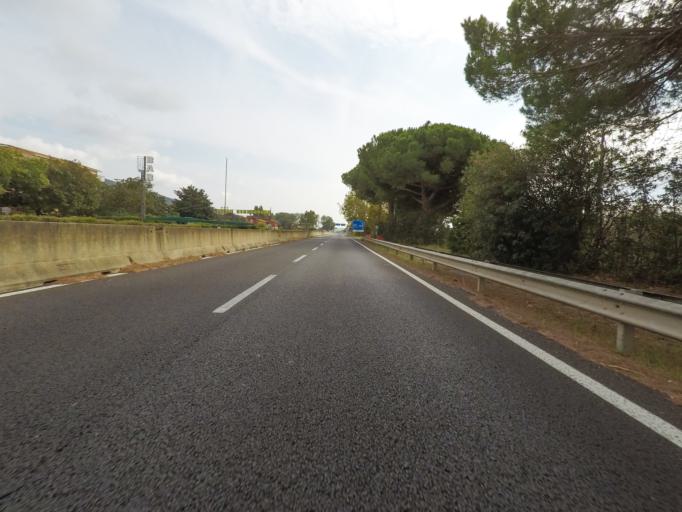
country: IT
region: Tuscany
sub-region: Provincia di Grosseto
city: Orbetello Scalo
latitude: 42.4745
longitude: 11.2334
